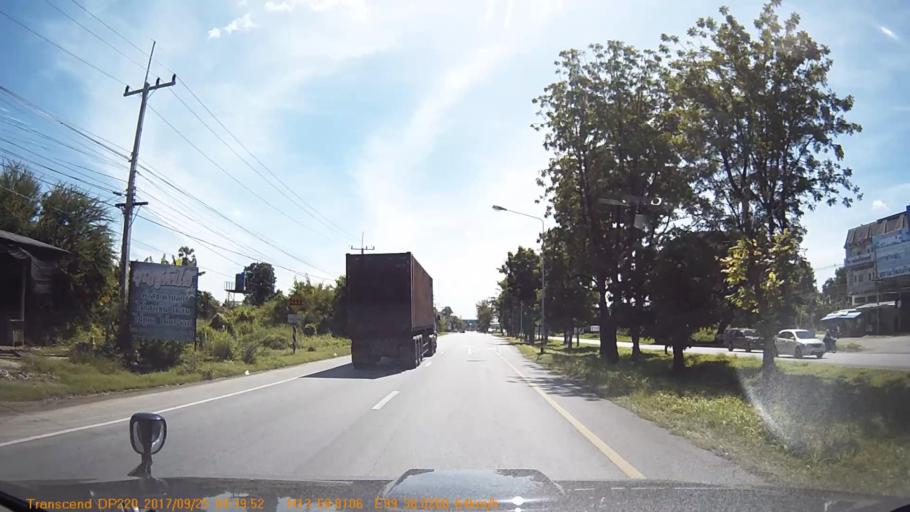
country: TH
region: Kanchanaburi
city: Tha Muang
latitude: 13.9801
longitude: 99.6340
